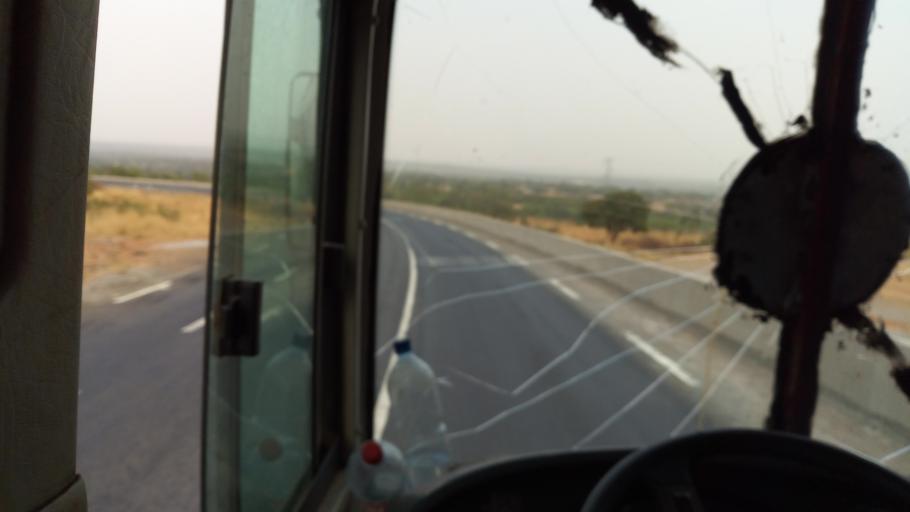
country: TG
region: Kara
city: Bafilo
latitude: 9.3486
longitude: 1.2707
